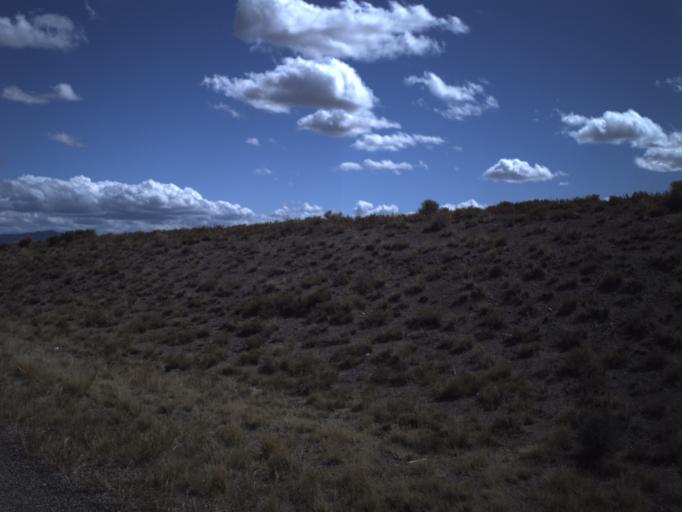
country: US
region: Utah
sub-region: Beaver County
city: Milford
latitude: 38.4380
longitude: -113.1483
